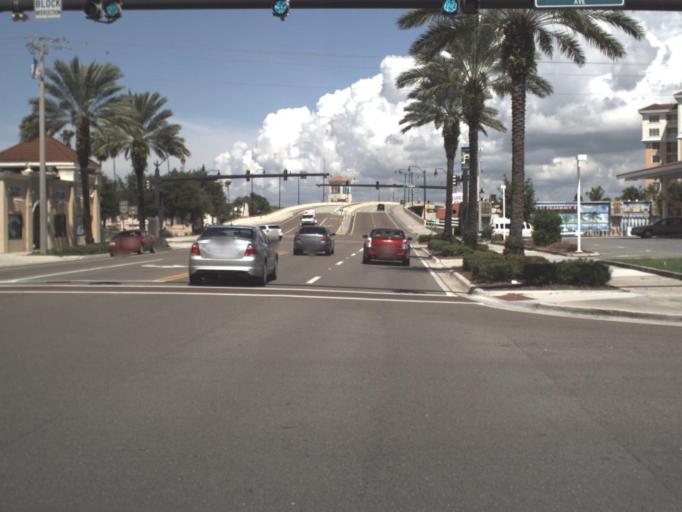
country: US
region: Florida
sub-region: Sarasota County
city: Venice
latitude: 27.0999
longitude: -82.4442
